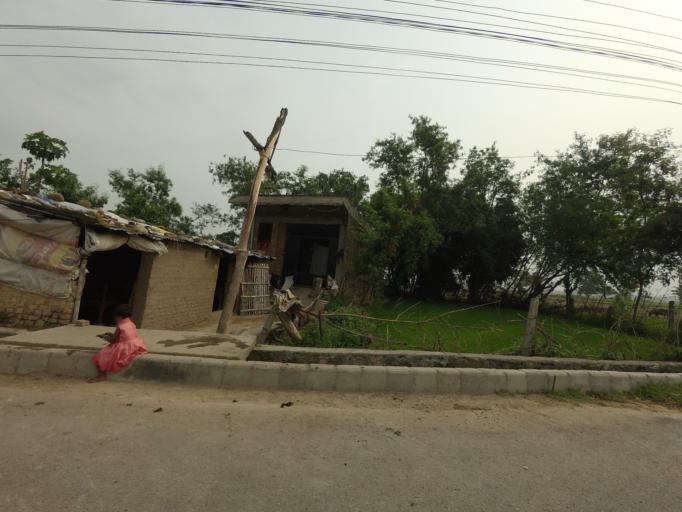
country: NP
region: Western Region
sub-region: Lumbini Zone
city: Bhairahawa
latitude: 27.4889
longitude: 83.4345
